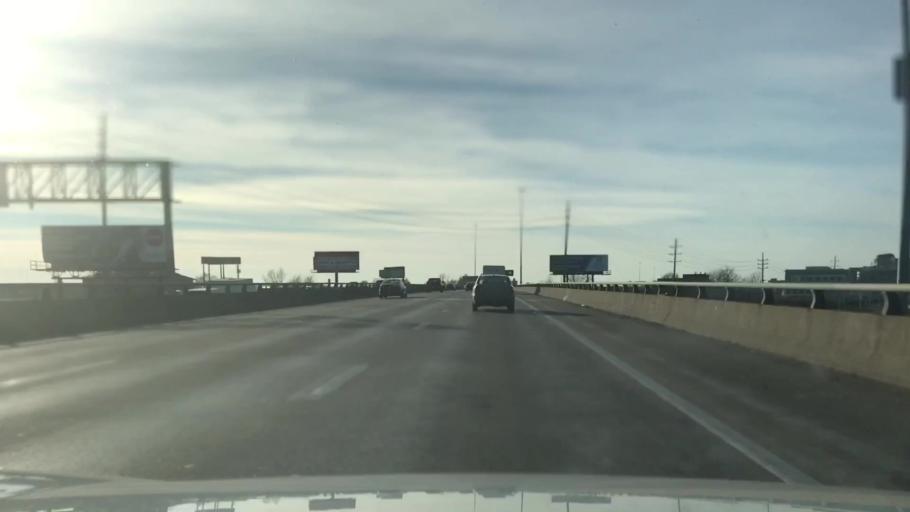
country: US
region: Missouri
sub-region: City of Saint Louis
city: St. Louis
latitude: 38.6327
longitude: -90.2437
